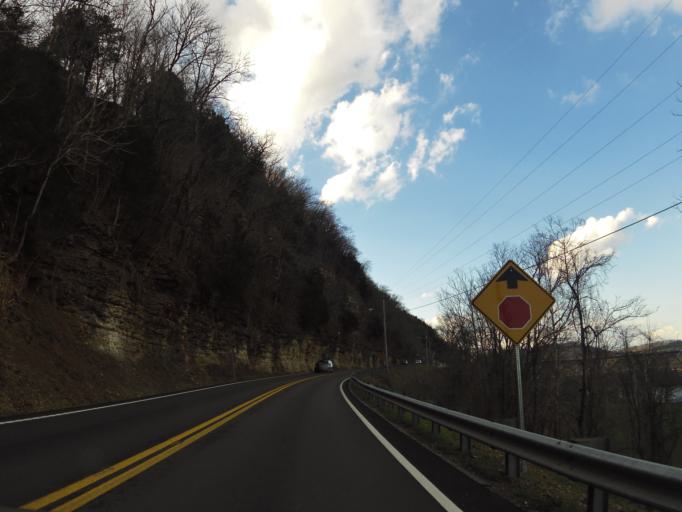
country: US
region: Tennessee
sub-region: Smith County
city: South Carthage
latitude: 36.2454
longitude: -85.9554
